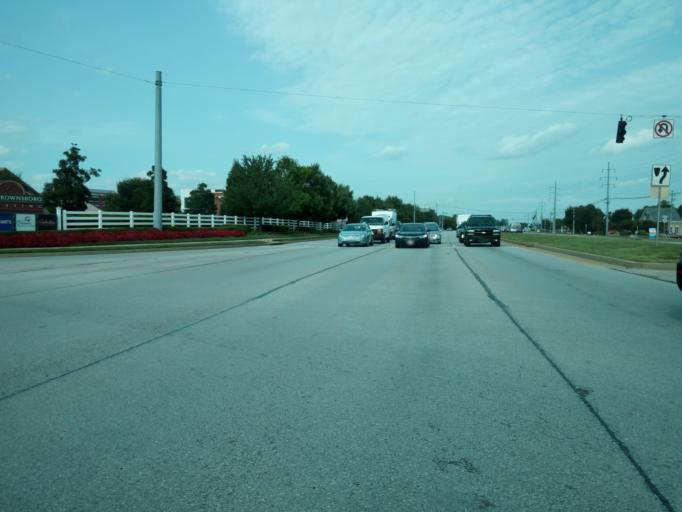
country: US
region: Kentucky
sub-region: Jefferson County
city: Worthington
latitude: 38.3111
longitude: -85.5703
